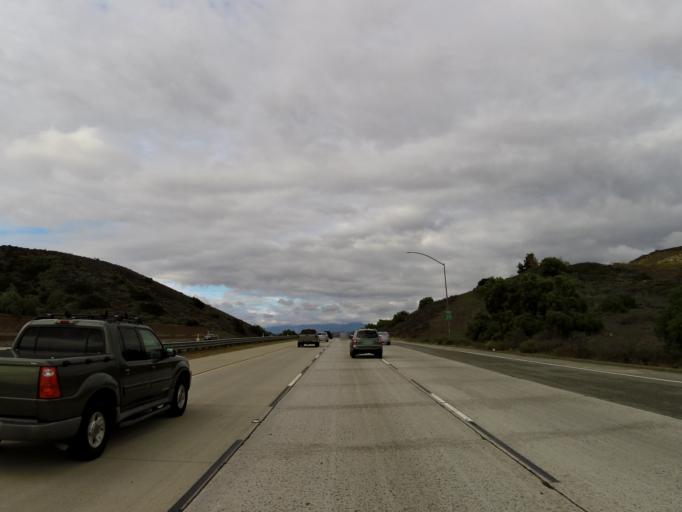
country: US
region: California
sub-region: Ventura County
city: Moorpark
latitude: 34.2698
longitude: -118.8535
